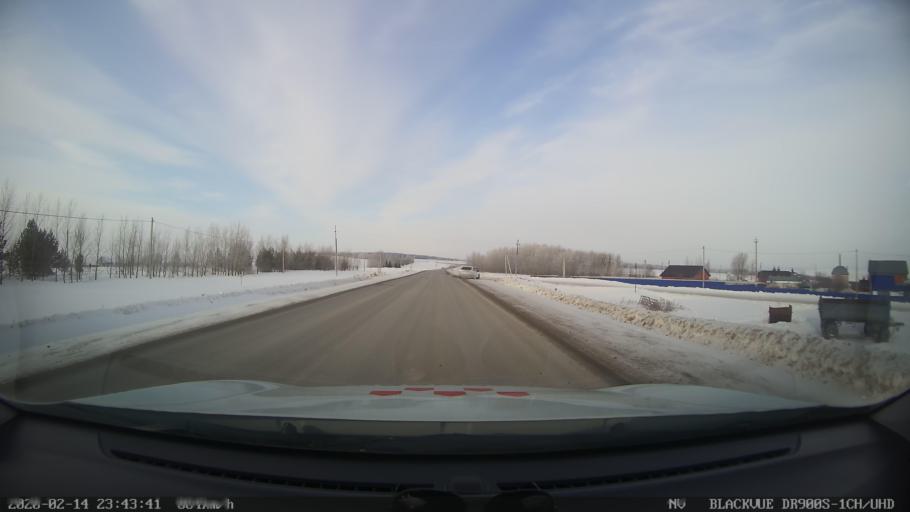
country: RU
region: Tatarstan
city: Kuybyshevskiy Zaton
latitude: 55.2048
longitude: 49.2488
